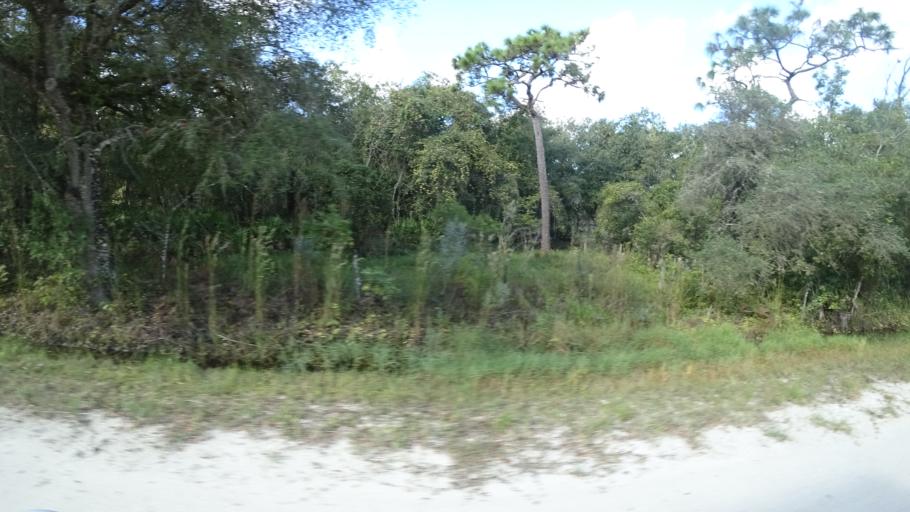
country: US
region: Florida
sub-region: Sarasota County
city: Lake Sarasota
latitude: 27.3255
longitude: -82.2050
